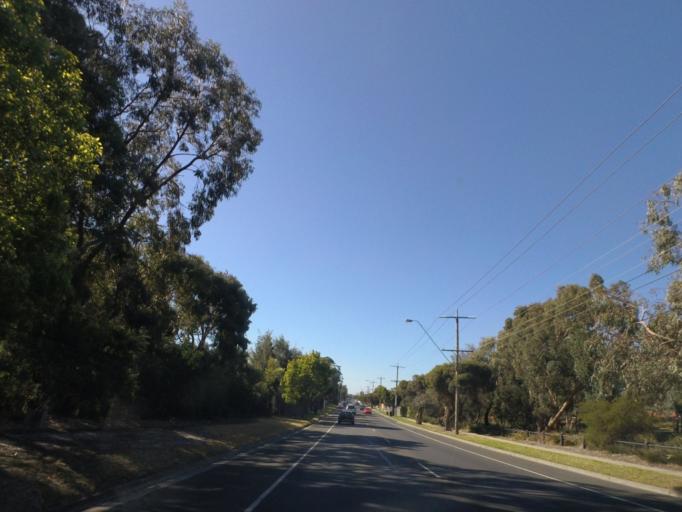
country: AU
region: Victoria
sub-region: Monash
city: Oakleigh South
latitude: -37.9199
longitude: 145.1019
